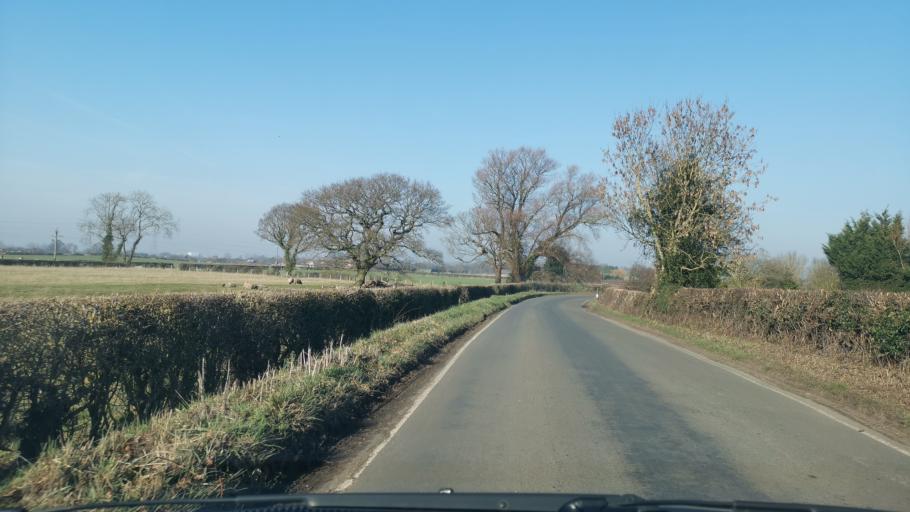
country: GB
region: England
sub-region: City of York
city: Murton
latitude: 53.9708
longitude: -1.0107
